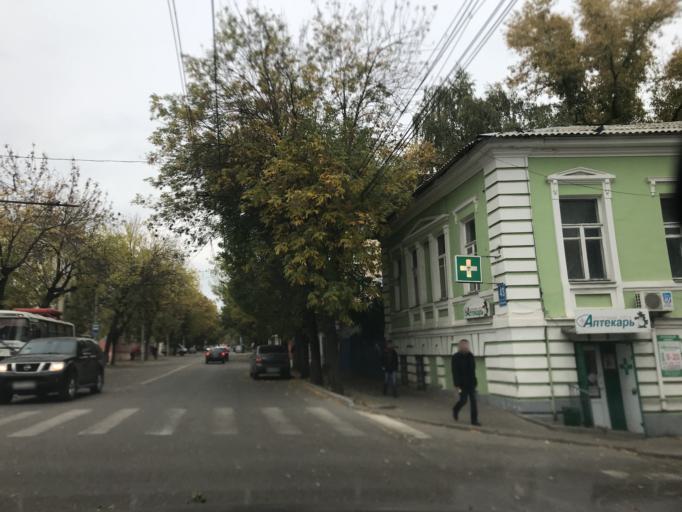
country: RU
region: Kaluga
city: Kaluga
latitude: 54.5054
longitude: 36.2622
